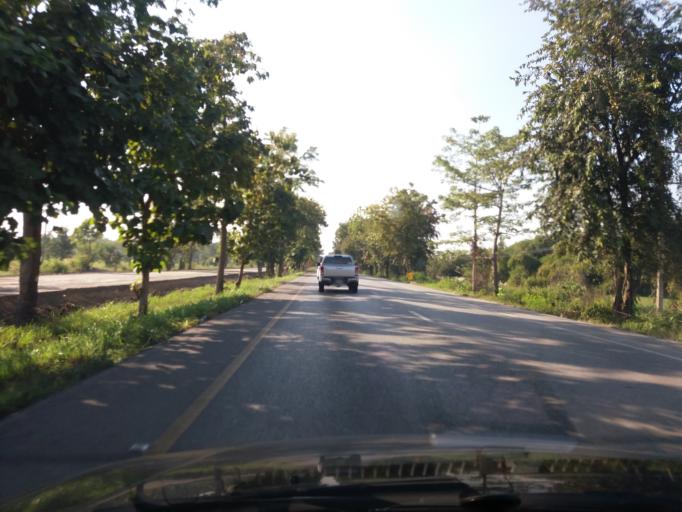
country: TH
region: Nakhon Sawan
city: Nakhon Sawan
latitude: 15.7376
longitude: 100.0208
